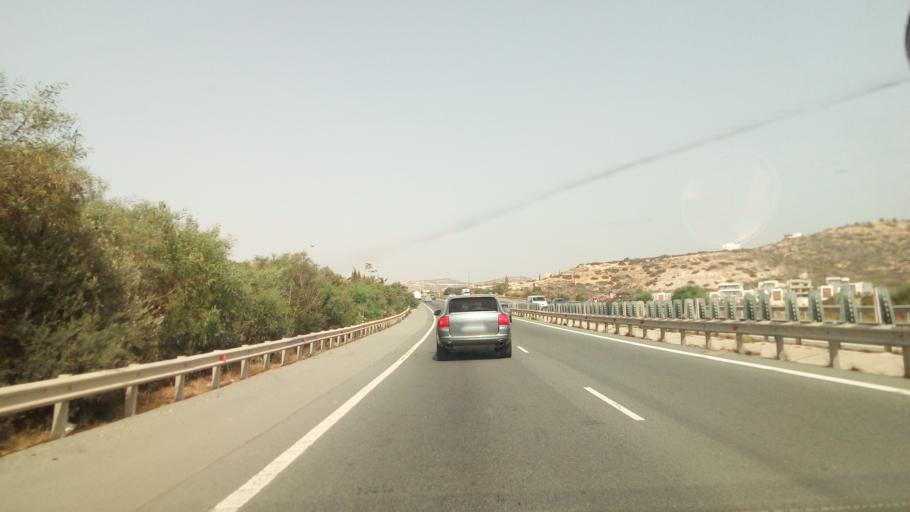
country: CY
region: Larnaka
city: Agios Tychon
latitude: 34.7175
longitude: 33.1550
